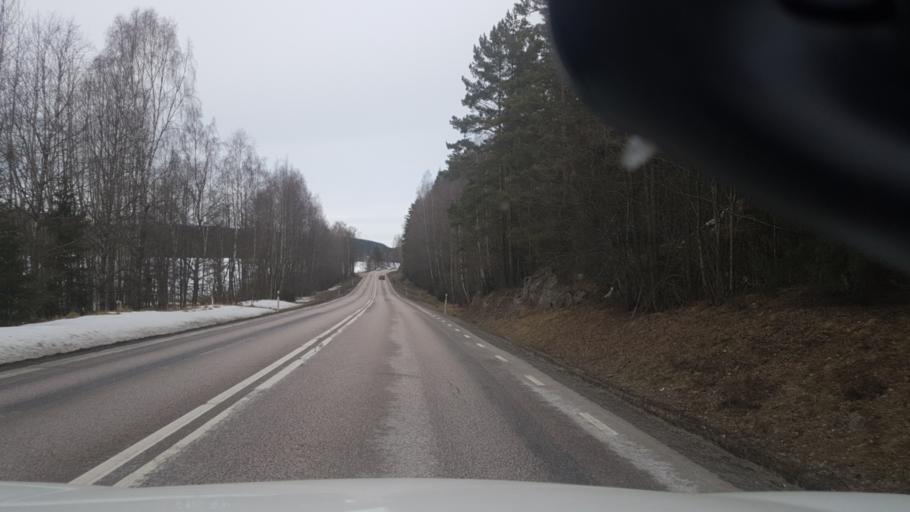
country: SE
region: Vaermland
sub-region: Eda Kommun
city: Amotfors
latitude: 59.7401
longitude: 12.4885
